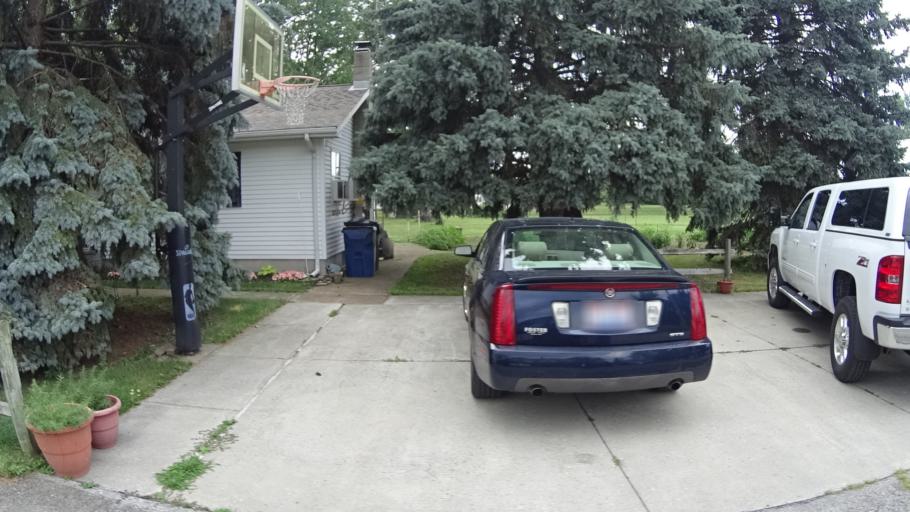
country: US
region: Ohio
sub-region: Erie County
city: Sandusky
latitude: 41.4415
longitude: -82.7436
